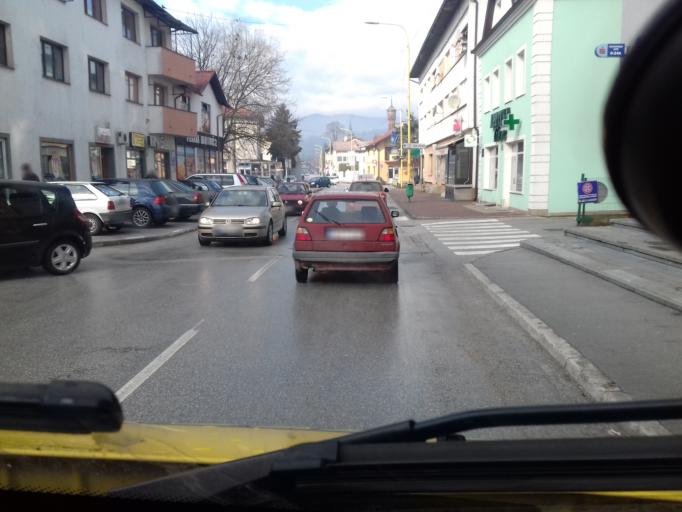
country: BA
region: Federation of Bosnia and Herzegovina
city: Zepce
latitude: 44.4240
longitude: 18.0352
